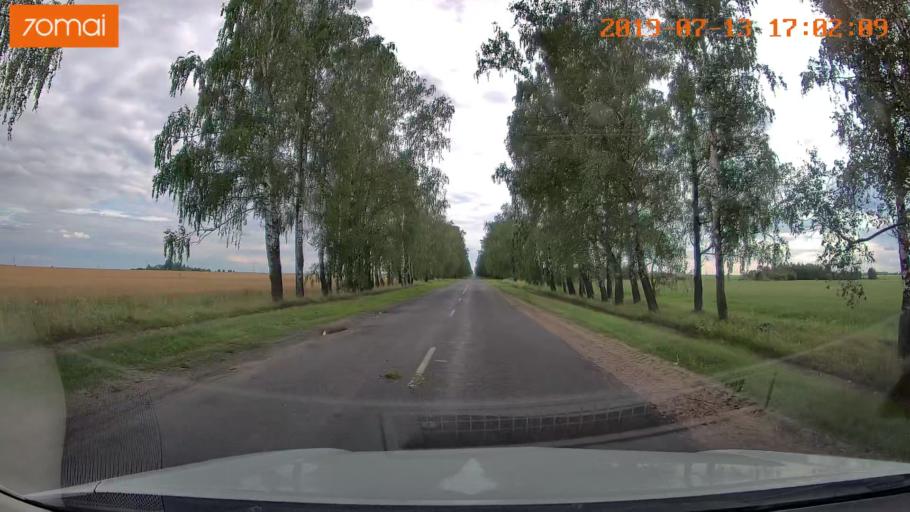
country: BY
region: Mogilev
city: Kirawsk
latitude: 53.2888
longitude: 29.3897
